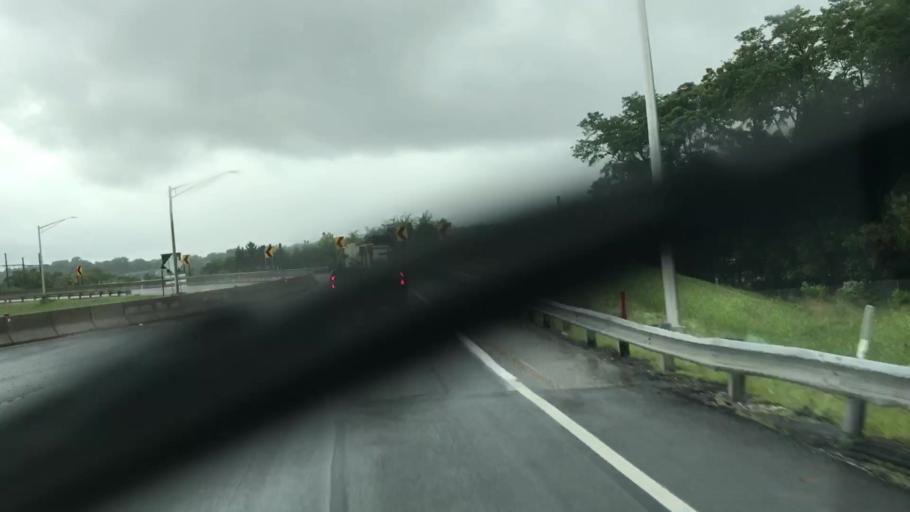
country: US
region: Pennsylvania
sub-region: Cumberland County
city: New Cumberland
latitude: 40.2121
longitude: -76.8709
